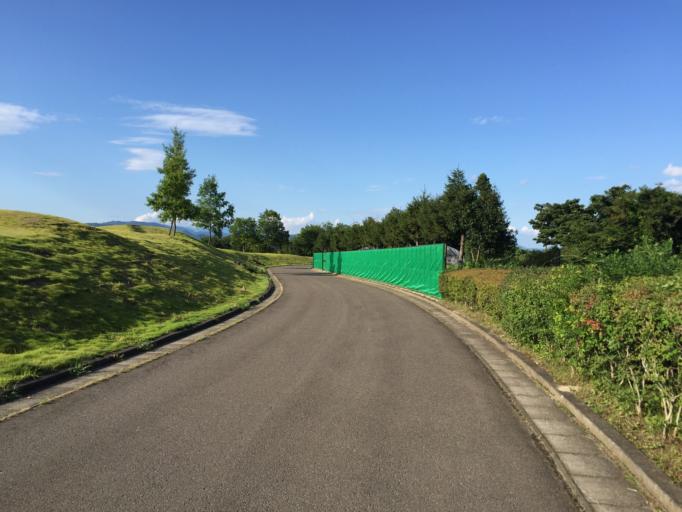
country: JP
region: Fukushima
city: Fukushima-shi
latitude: 37.7154
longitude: 140.3581
